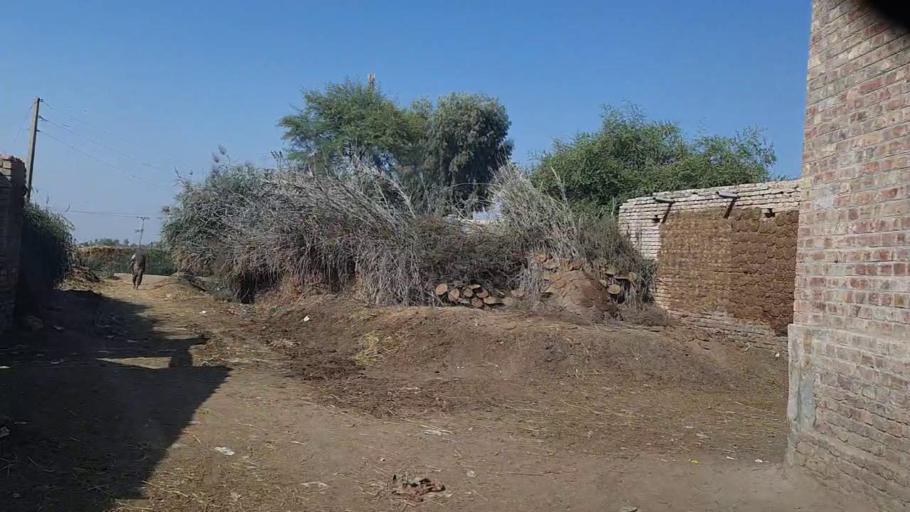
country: PK
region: Sindh
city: Tangwani
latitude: 28.2375
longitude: 68.9296
